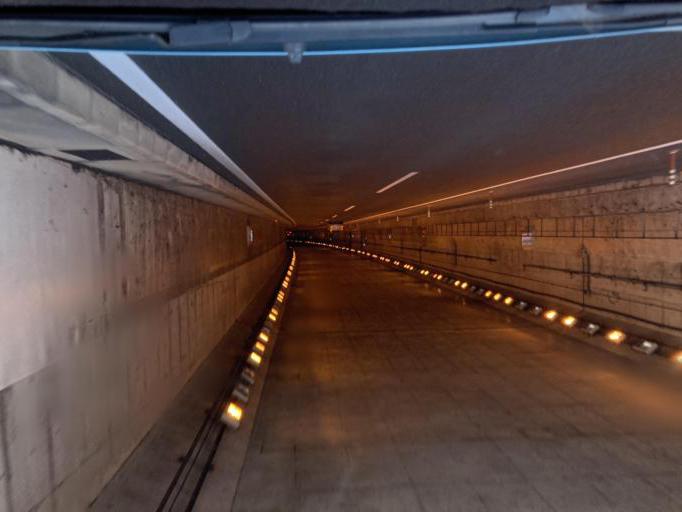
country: JP
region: Okinawa
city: Naha-shi
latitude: 26.2184
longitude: 127.6636
